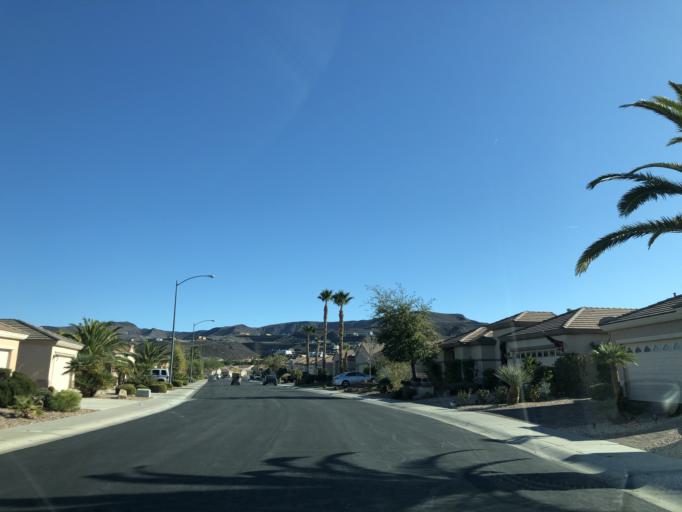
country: US
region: Nevada
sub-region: Clark County
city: Whitney
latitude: 36.0042
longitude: -115.0719
